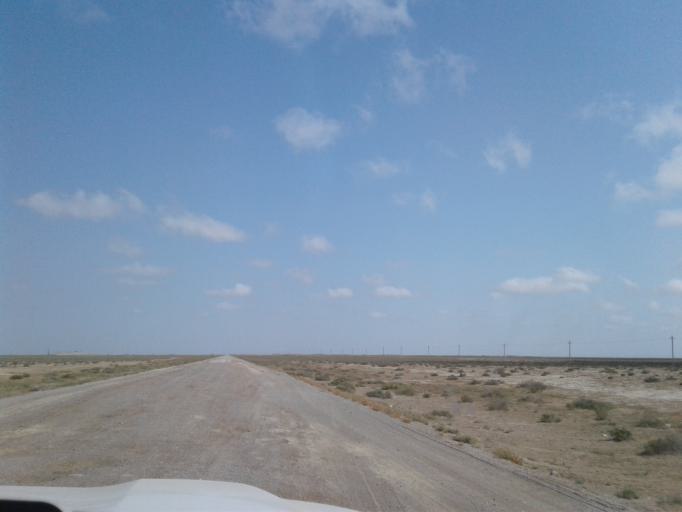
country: IR
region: Golestan
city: Gomishan
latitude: 37.6625
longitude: 53.9336
